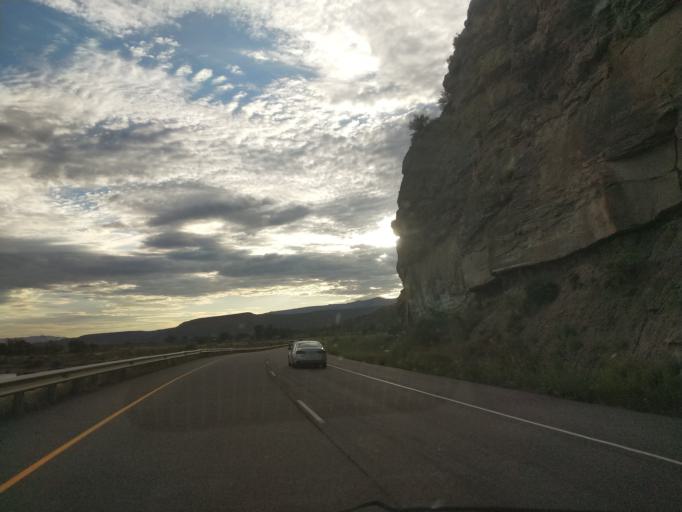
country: US
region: Colorado
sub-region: Mesa County
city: Palisade
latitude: 39.2839
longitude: -108.2295
